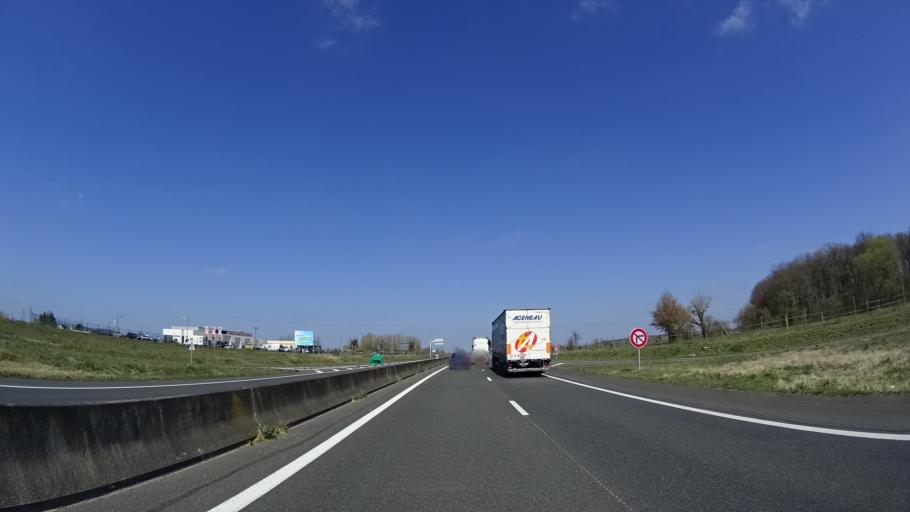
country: FR
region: Pays de la Loire
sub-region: Departement de Maine-et-Loire
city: Saint-Jean
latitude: 47.2564
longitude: -0.3333
